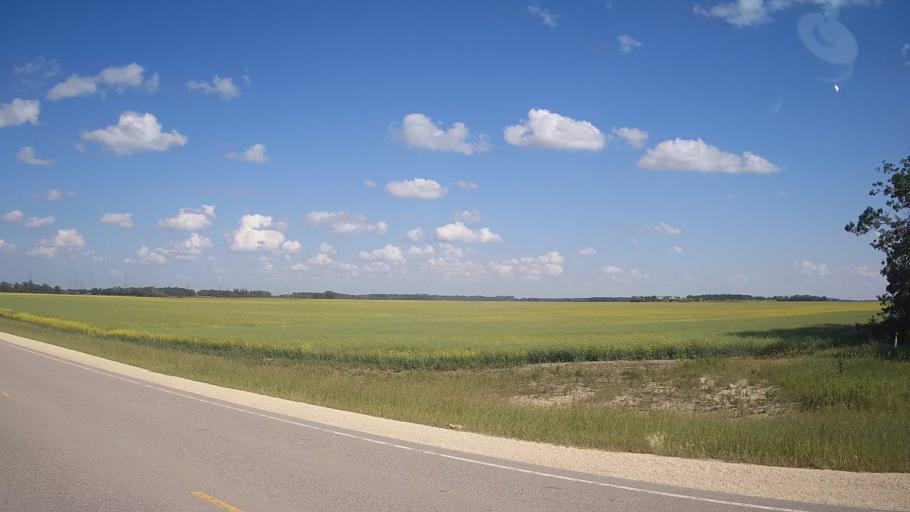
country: CA
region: Manitoba
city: Stonewall
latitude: 50.1228
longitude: -97.5053
